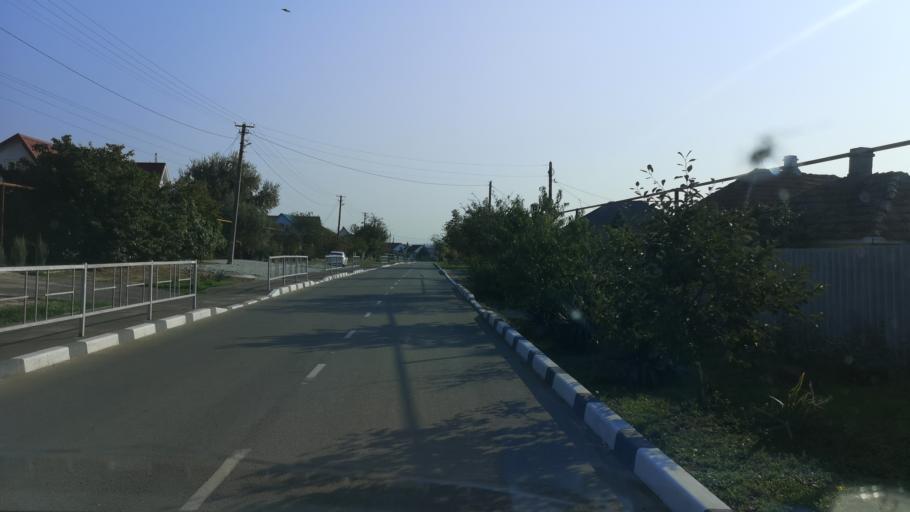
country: RU
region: Krasnodarskiy
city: Taman'
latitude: 45.2138
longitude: 36.6998
